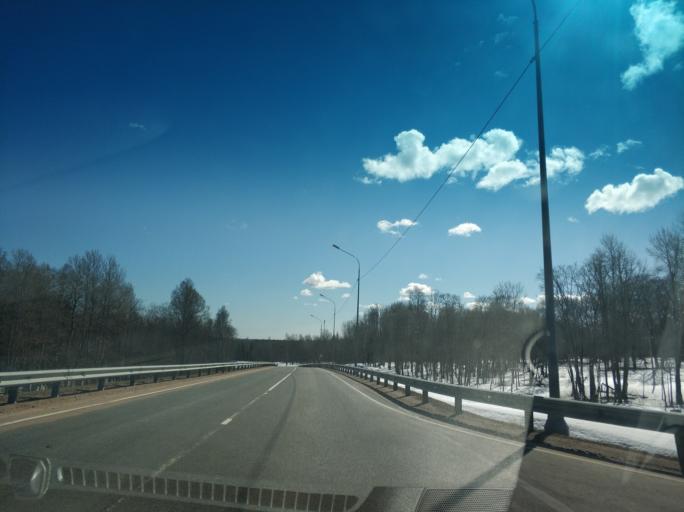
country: RU
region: Leningrad
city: Sosnovo
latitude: 60.4324
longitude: 30.2368
